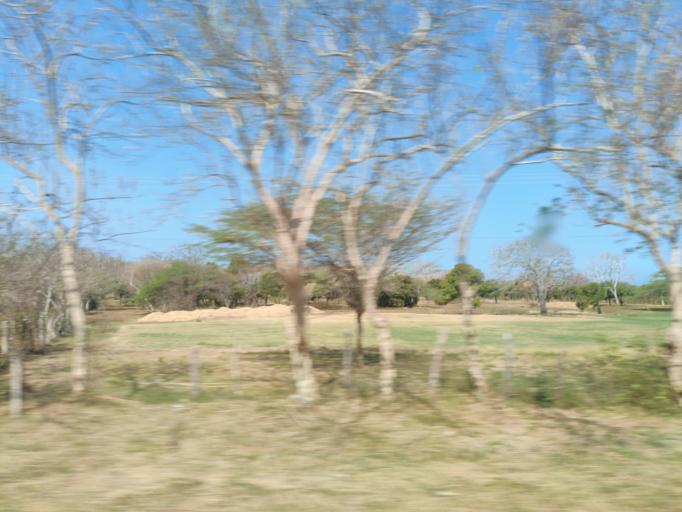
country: CO
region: Atlantico
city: Juan de Acosta
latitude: 10.8517
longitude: -75.1277
